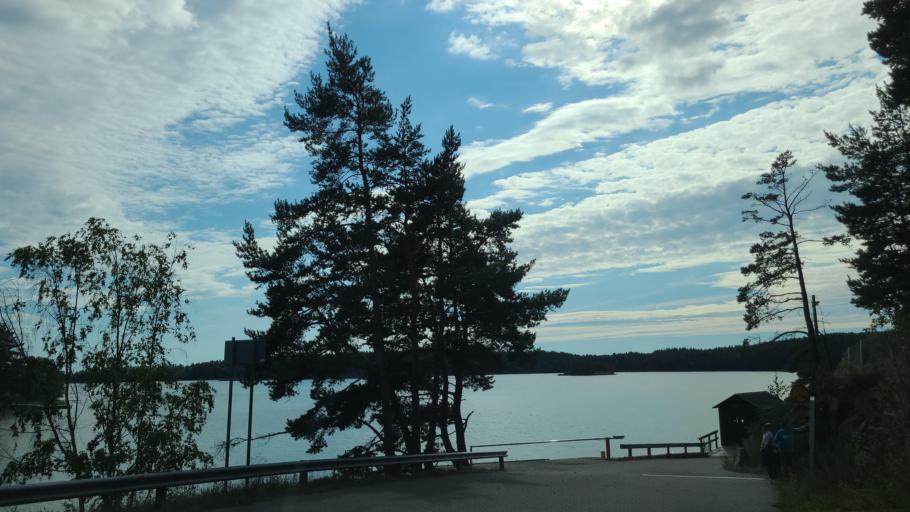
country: FI
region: Varsinais-Suomi
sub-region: Turku
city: Rymaettylae
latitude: 60.2859
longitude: 21.9696
